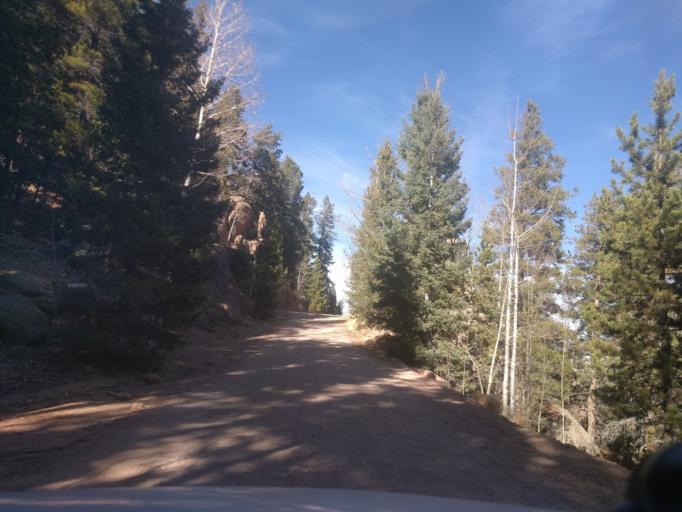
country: US
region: Colorado
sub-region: Douglas County
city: Perry Park
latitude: 39.1993
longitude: -105.0515
